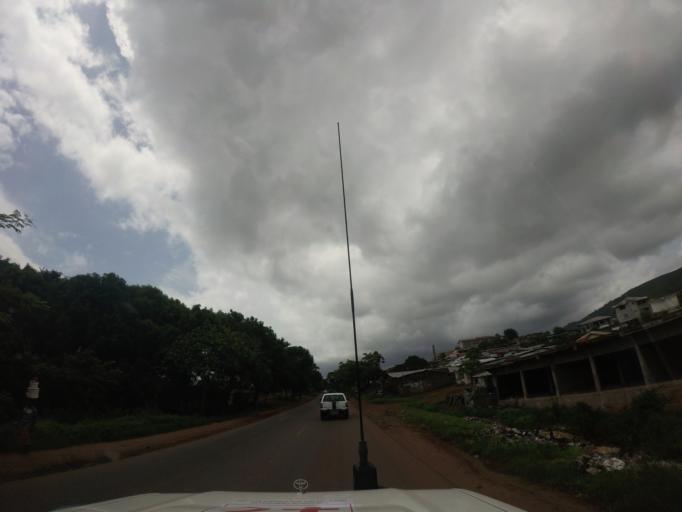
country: SL
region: Western Area
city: Waterloo
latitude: 8.3683
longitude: -13.0914
